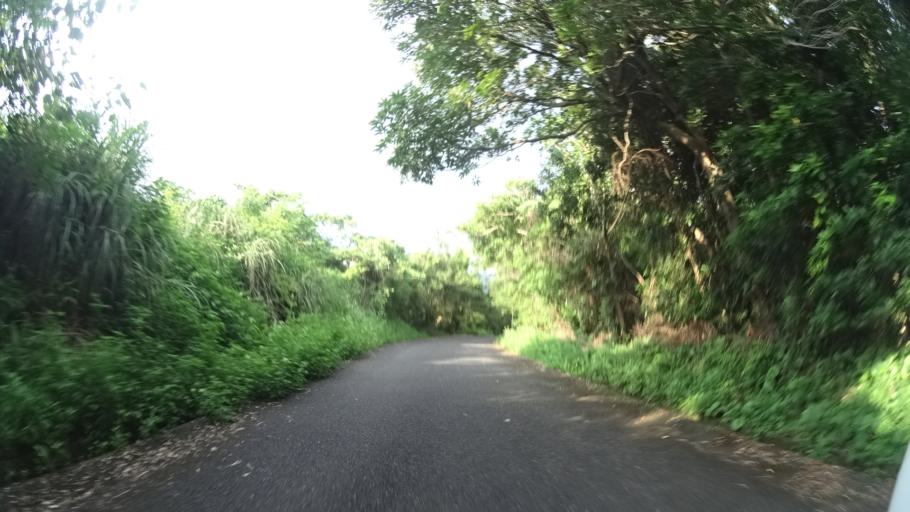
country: JP
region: Kagoshima
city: Nishinoomote
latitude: 30.2323
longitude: 130.4855
